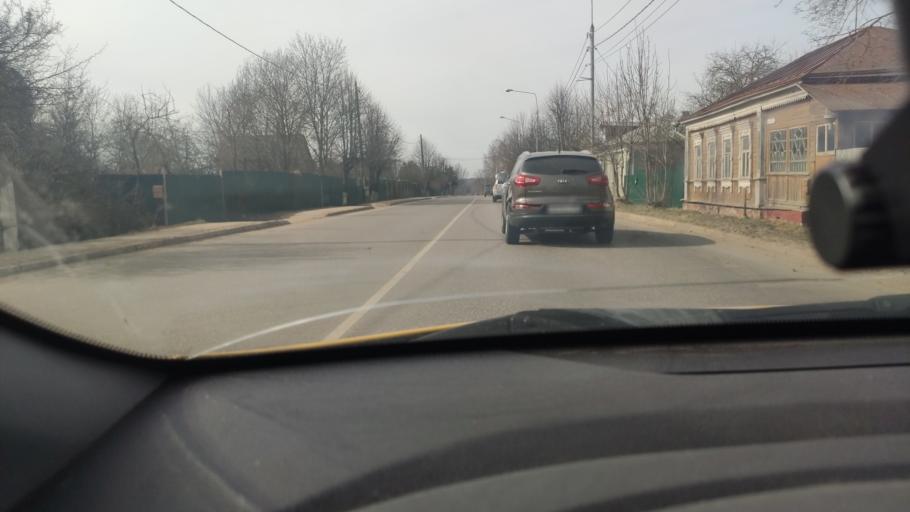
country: RU
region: Moskovskaya
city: Ruza
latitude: 55.6958
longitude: 36.2037
